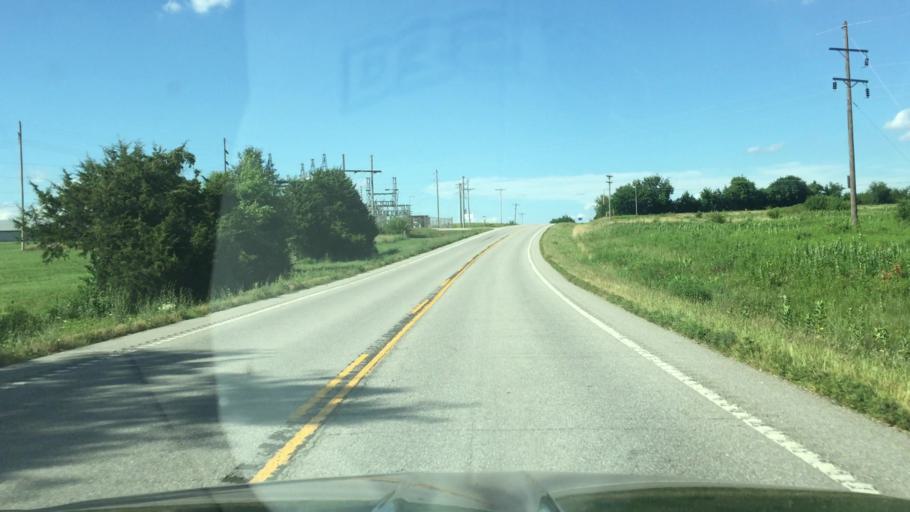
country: US
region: Missouri
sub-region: Morgan County
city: Versailles
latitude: 38.5242
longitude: -92.8020
